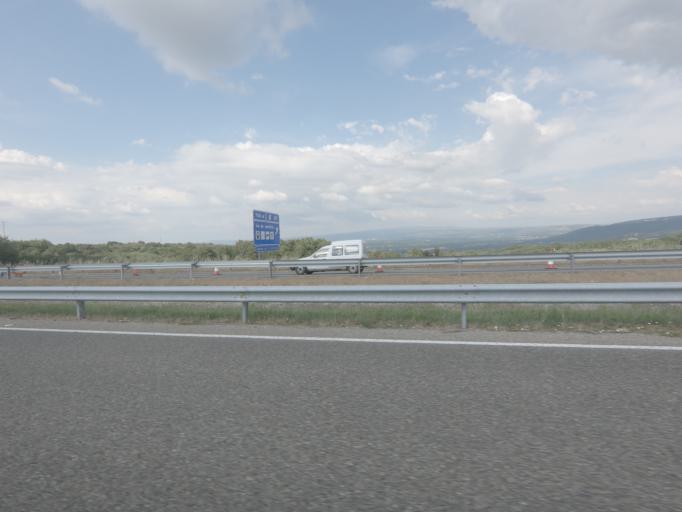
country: ES
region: Galicia
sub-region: Provincia de Ourense
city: Taboadela
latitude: 42.2387
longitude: -7.8581
